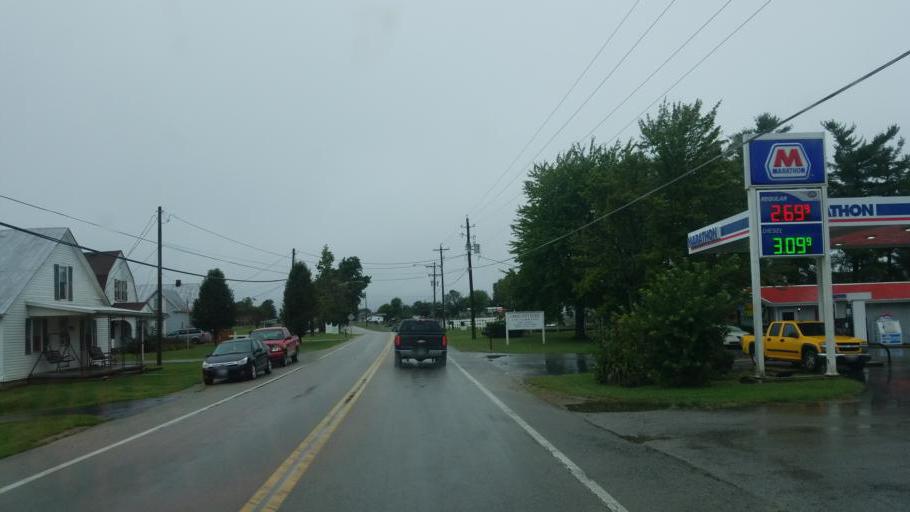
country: US
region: Ohio
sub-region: Adams County
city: West Union
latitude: 38.7975
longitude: -83.5283
